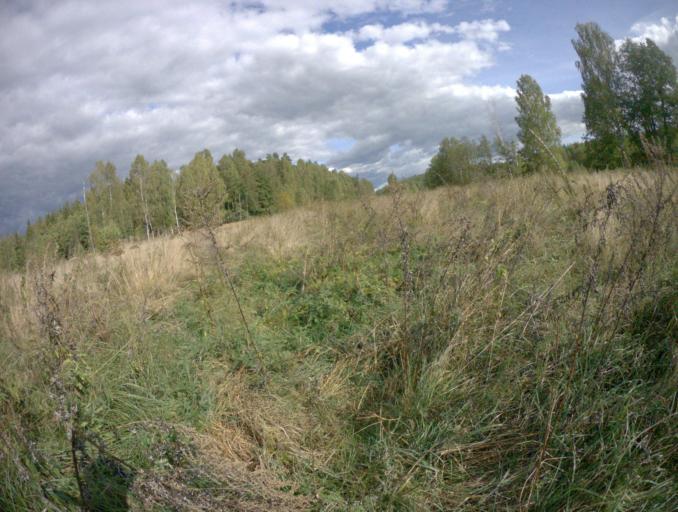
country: RU
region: Vladimir
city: Golovino
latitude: 55.8912
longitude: 40.4254
